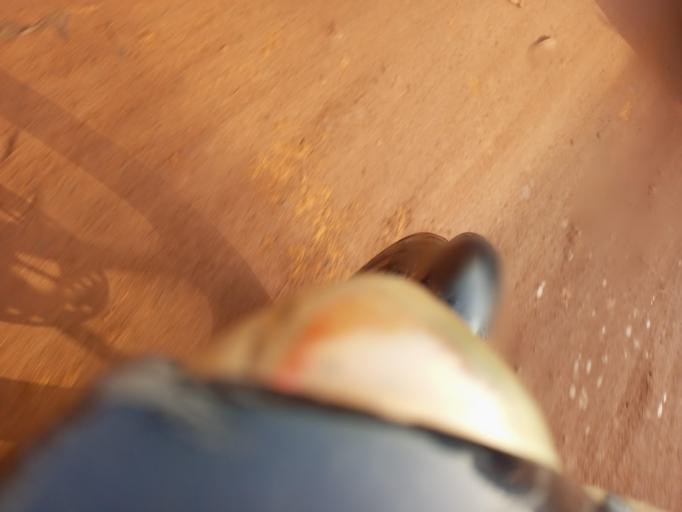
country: ML
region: Bamako
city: Bamako
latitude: 12.5261
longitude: -7.9949
